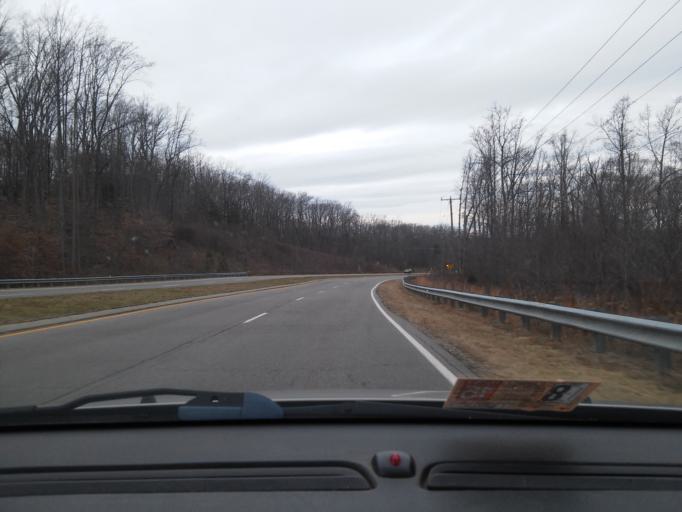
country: US
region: Virginia
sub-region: Chesterfield County
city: Bon Air
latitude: 37.5431
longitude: -77.6499
